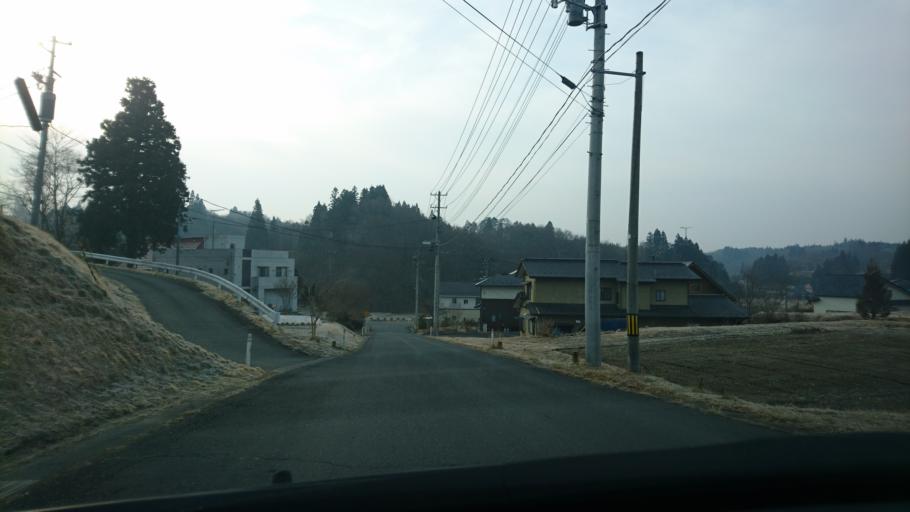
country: JP
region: Iwate
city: Ichinoseki
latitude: 38.9117
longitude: 141.3406
